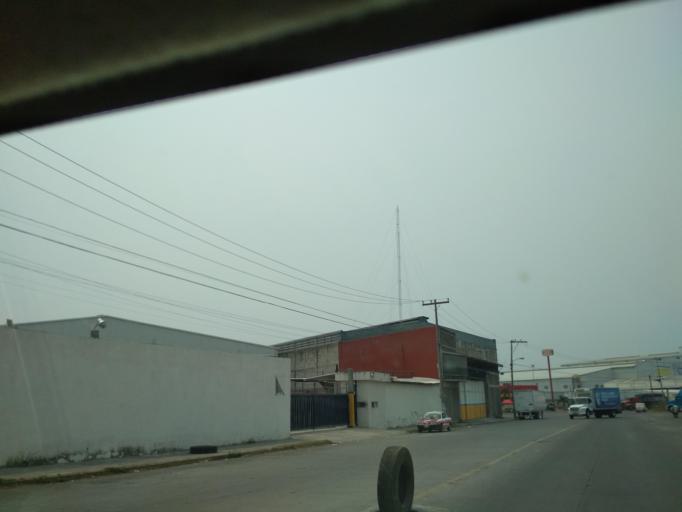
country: MX
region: Veracruz
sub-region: Veracruz
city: Las Amapolas
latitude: 19.1625
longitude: -96.2261
